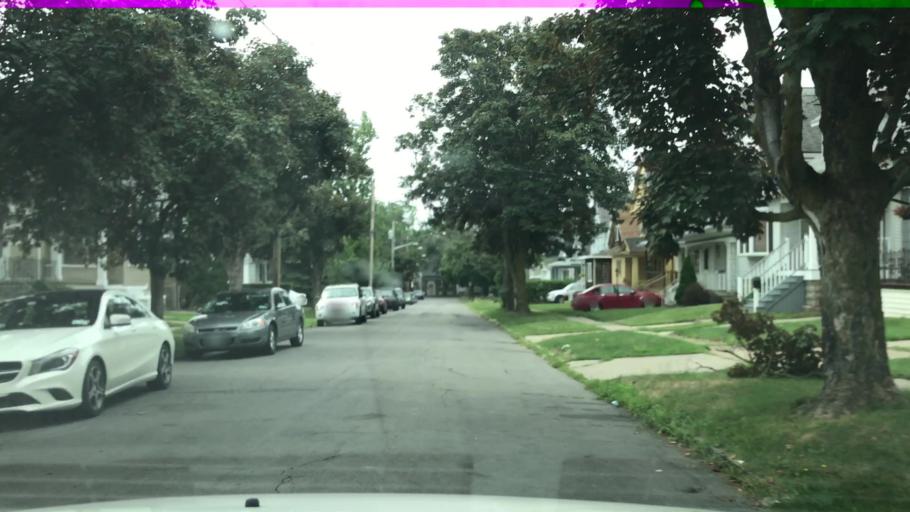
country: US
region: New York
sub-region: Erie County
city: Sloan
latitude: 42.9082
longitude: -78.7998
